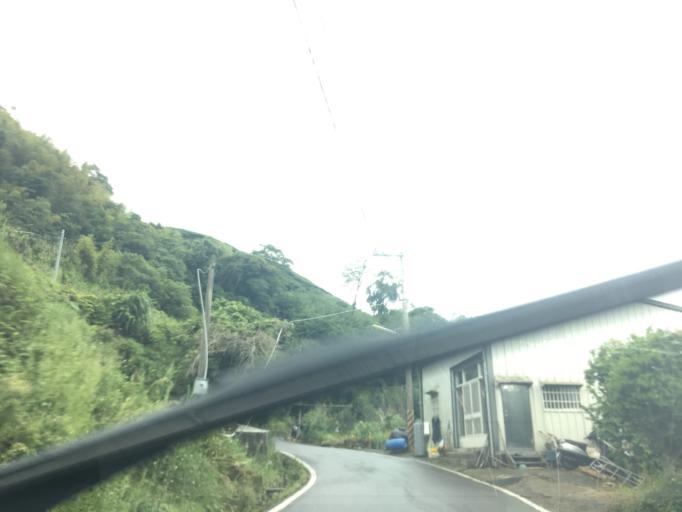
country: TW
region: Taiwan
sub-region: Yunlin
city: Douliu
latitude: 23.5611
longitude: 120.6614
